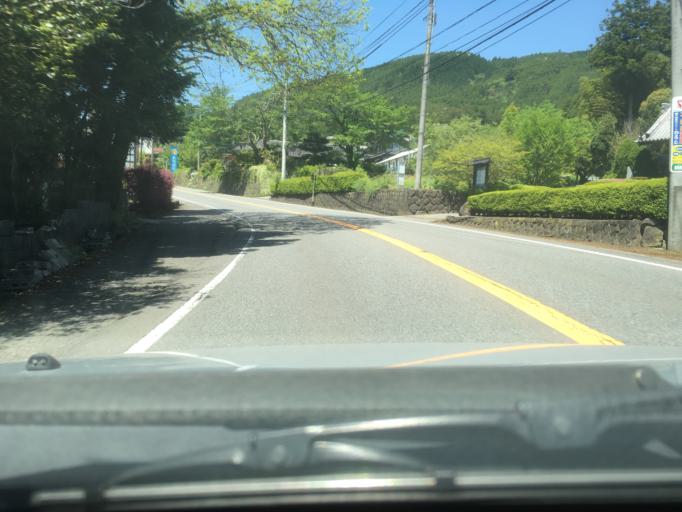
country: JP
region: Oita
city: Beppu
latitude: 33.2659
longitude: 131.3538
